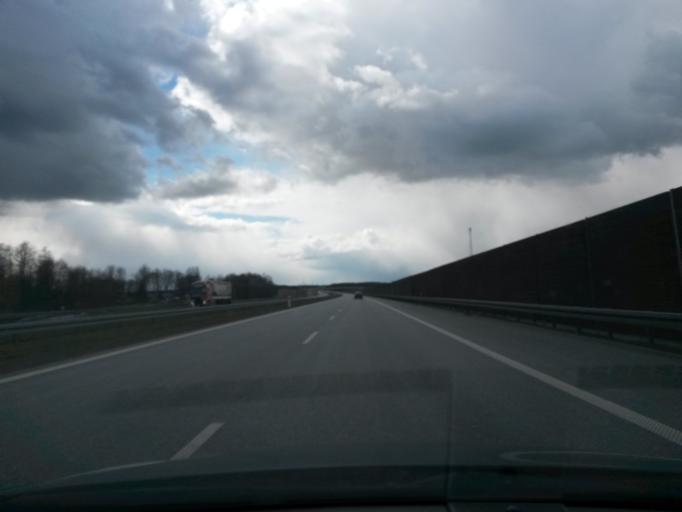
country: PL
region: Greater Poland Voivodeship
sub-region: Powiat koninski
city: Krzymow
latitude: 52.1426
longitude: 18.3898
